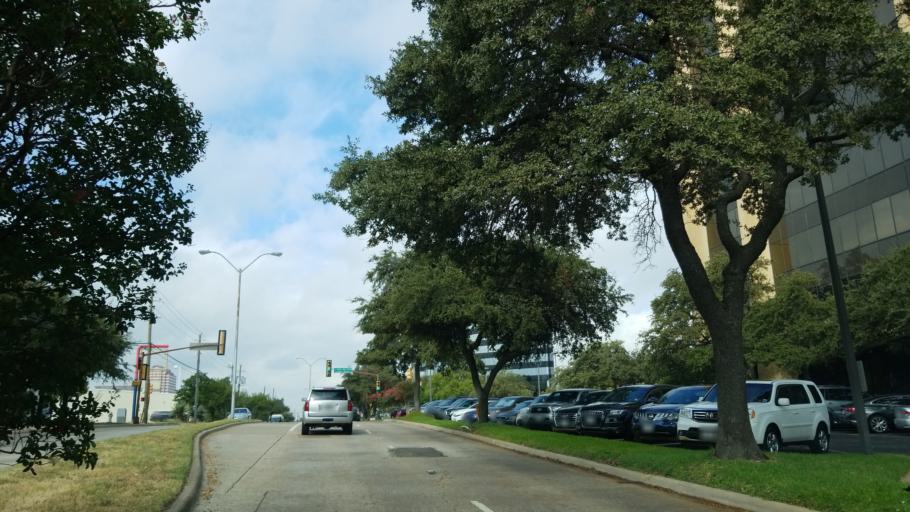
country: US
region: Texas
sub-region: Dallas County
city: Addison
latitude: 32.9328
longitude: -96.8065
